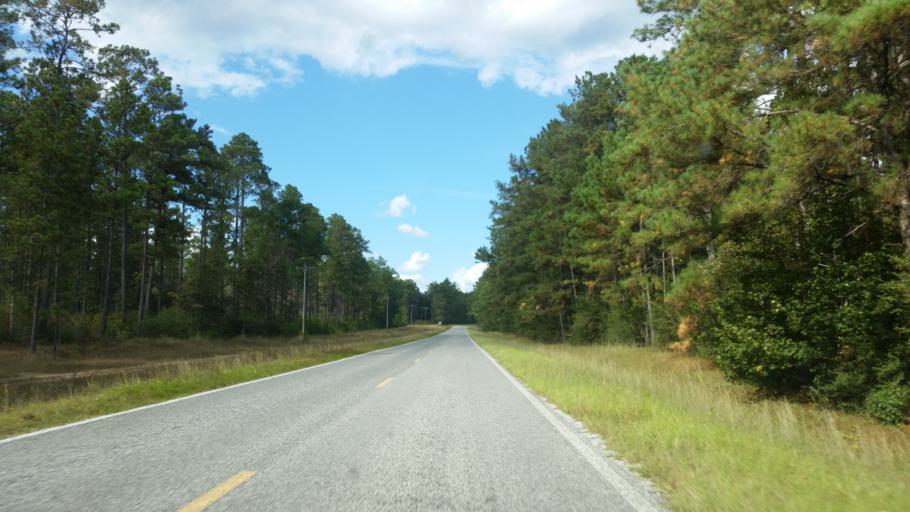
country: US
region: Mississippi
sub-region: Stone County
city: Wiggins
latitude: 30.9739
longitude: -89.0566
